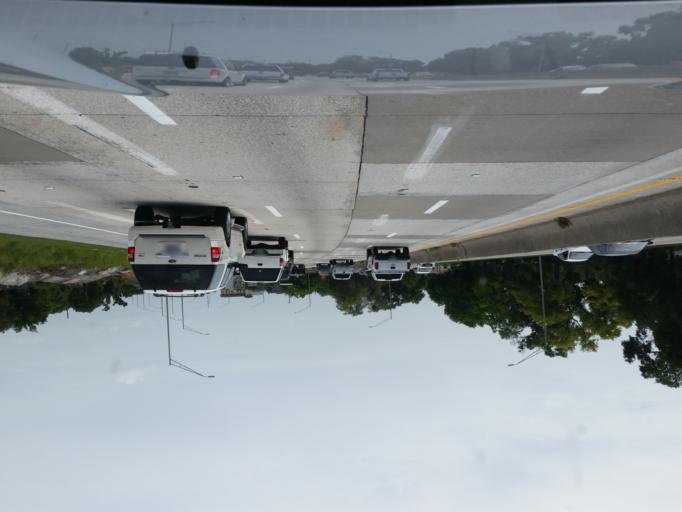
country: US
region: Florida
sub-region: Orange County
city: Fairview Shores
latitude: 28.5868
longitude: -81.3756
